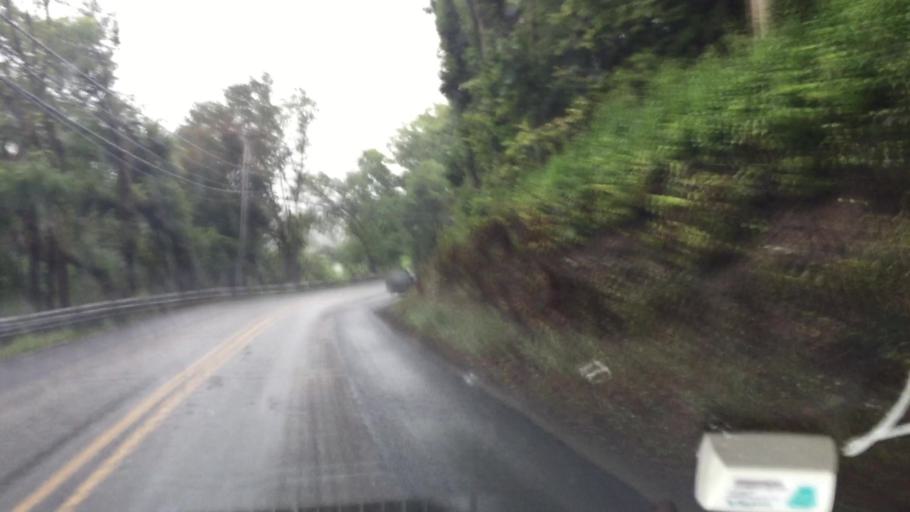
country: US
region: Pennsylvania
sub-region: Allegheny County
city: Ben Avon
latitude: 40.5324
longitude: -80.0643
